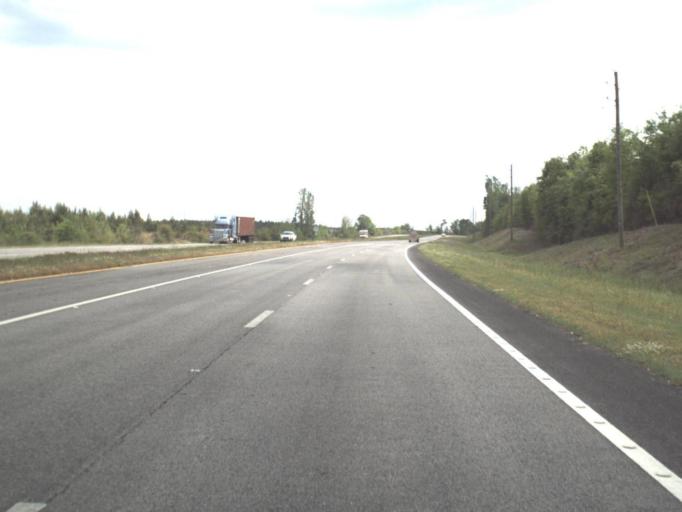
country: US
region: Florida
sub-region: Escambia County
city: Molino
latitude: 30.7951
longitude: -87.3341
